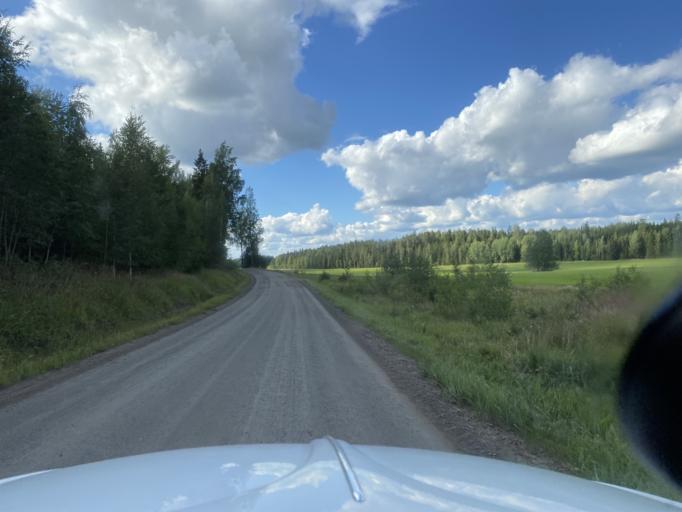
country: FI
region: Pirkanmaa
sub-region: Lounais-Pirkanmaa
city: Punkalaidun
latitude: 61.1211
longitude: 23.2671
